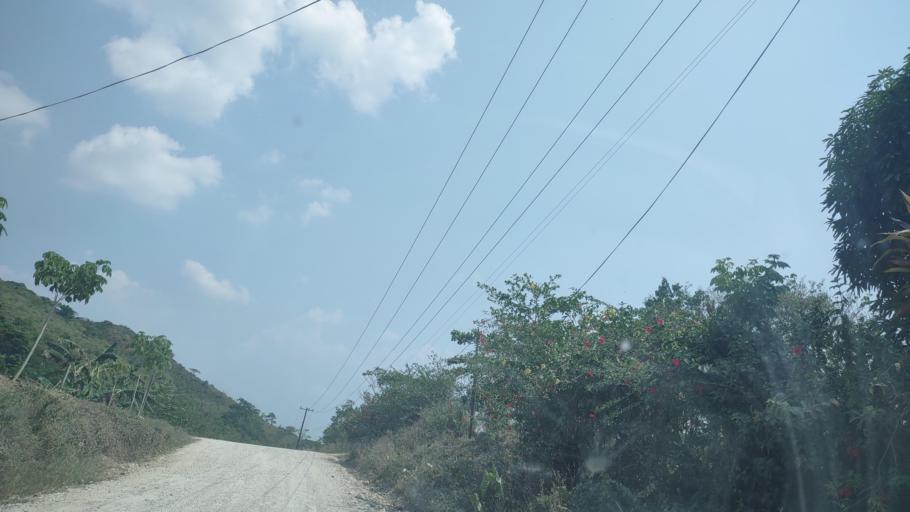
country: MX
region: Tabasco
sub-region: Huimanguillo
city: Francisco Rueda
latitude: 17.5698
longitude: -93.8867
